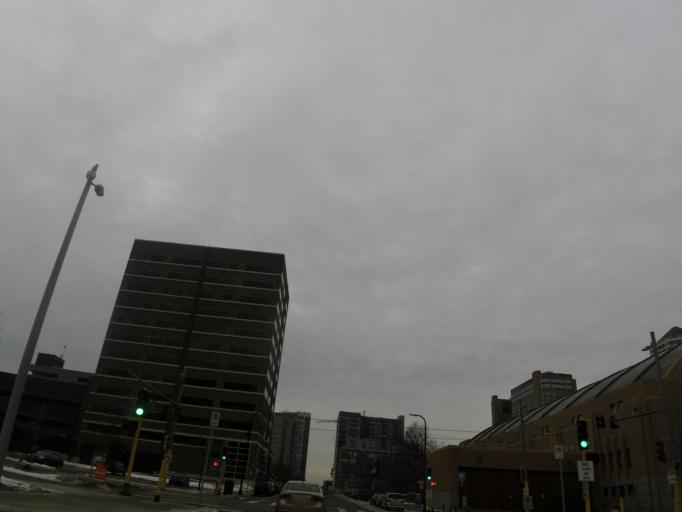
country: US
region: Minnesota
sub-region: Hennepin County
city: Minneapolis
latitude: 44.9756
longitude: -93.2622
